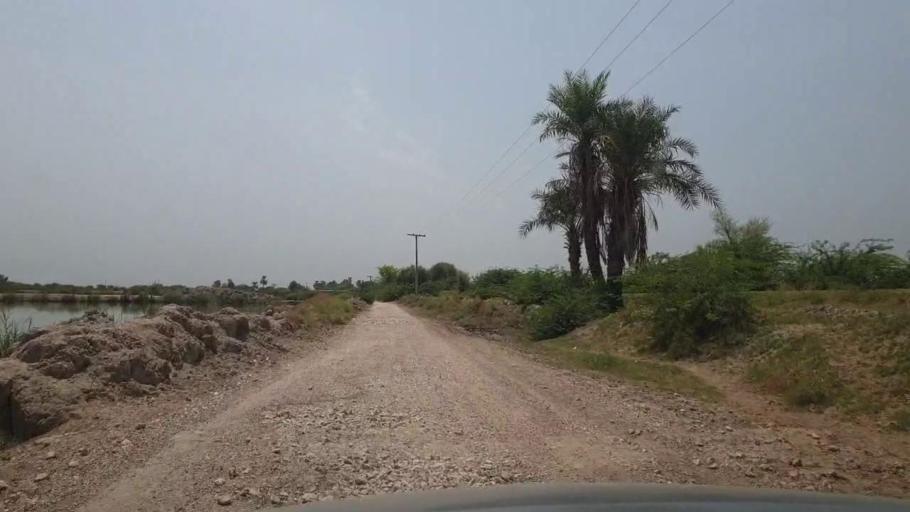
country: PK
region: Sindh
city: Garhi Yasin
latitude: 27.8827
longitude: 68.4954
